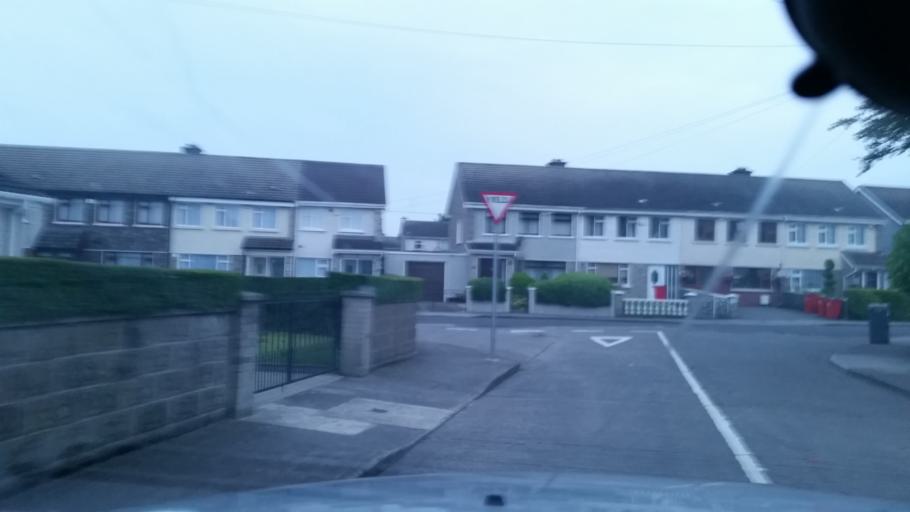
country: IE
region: Leinster
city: Beaumont
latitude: 53.3953
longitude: -6.2438
